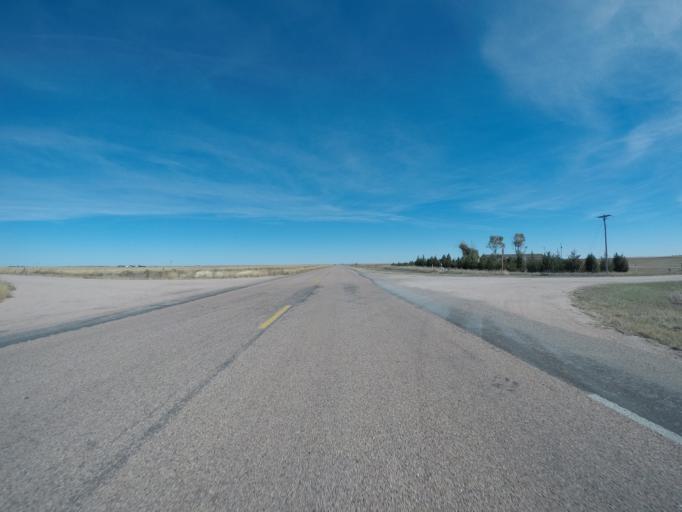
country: US
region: Colorado
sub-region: Yuma County
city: Yuma
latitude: 39.6561
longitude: -102.6121
